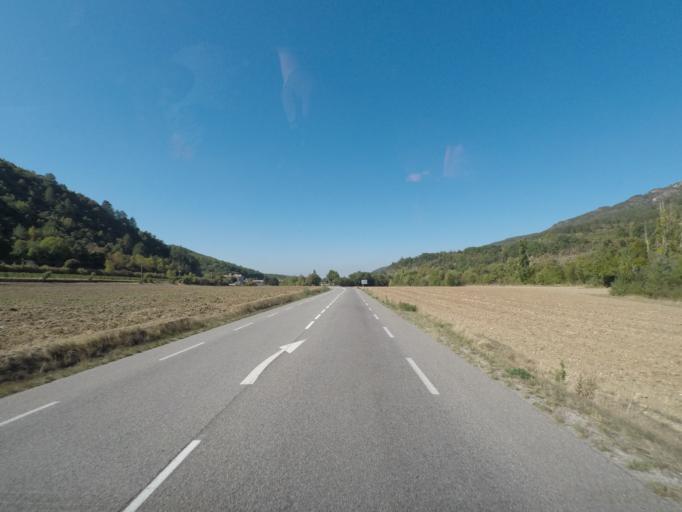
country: FR
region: Rhone-Alpes
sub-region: Departement de la Drome
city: Aouste-sur-Sye
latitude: 44.6923
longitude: 5.1798
